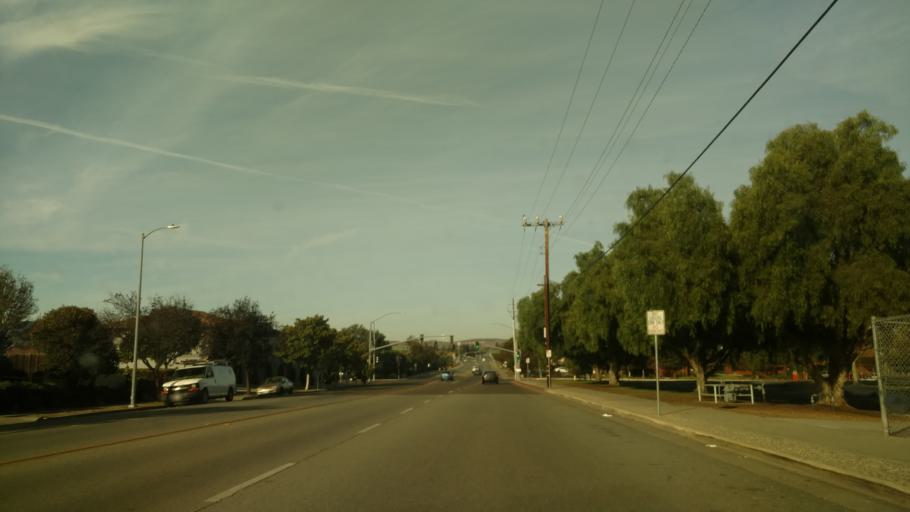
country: US
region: California
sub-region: San Benito County
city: Hollister
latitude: 36.8390
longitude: -121.3830
